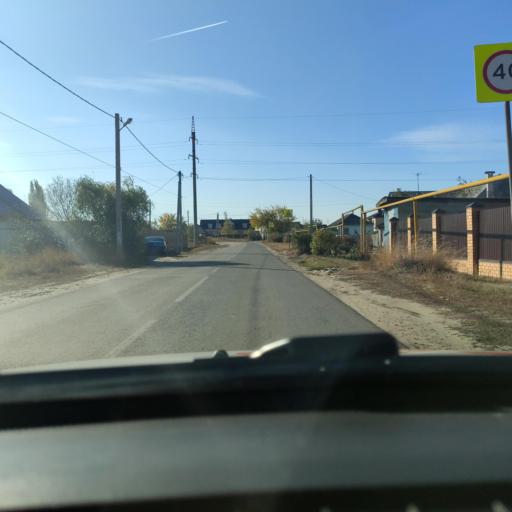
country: RU
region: Voronezj
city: Shilovo
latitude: 51.5218
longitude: 39.1466
